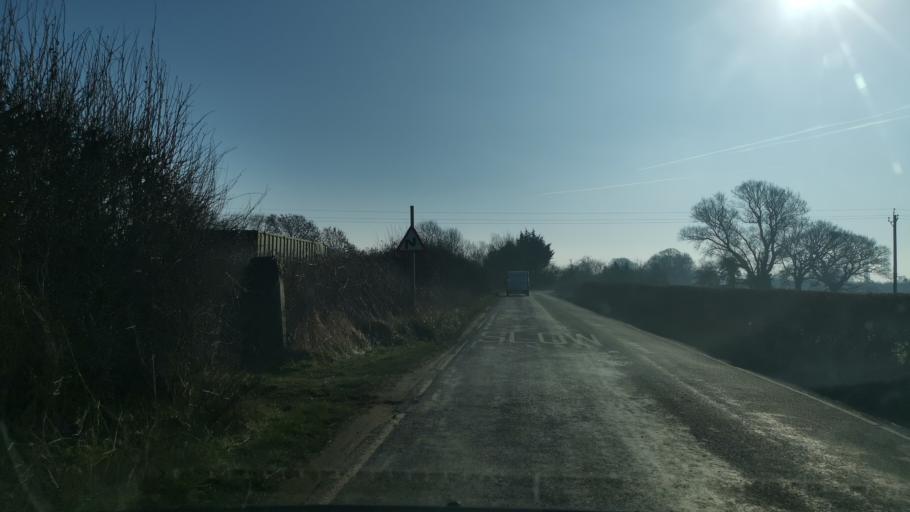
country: GB
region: England
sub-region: City of York
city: Murton
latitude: 53.9725
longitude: -1.0122
